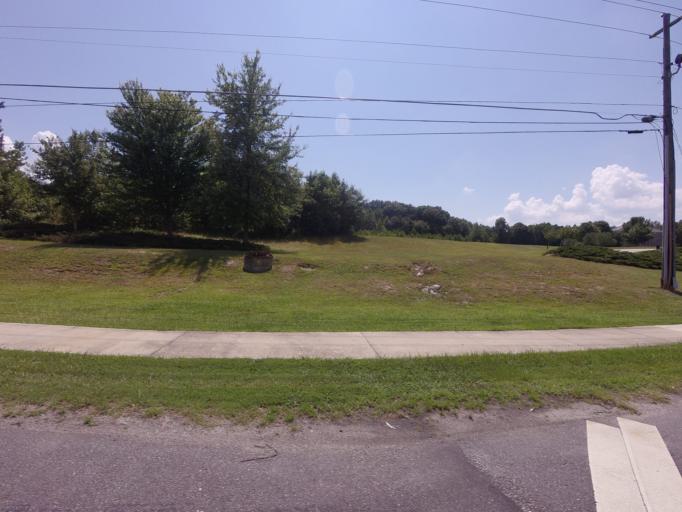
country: US
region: Georgia
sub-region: Fulton County
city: Johns Creek
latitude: 34.0108
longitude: -84.1834
